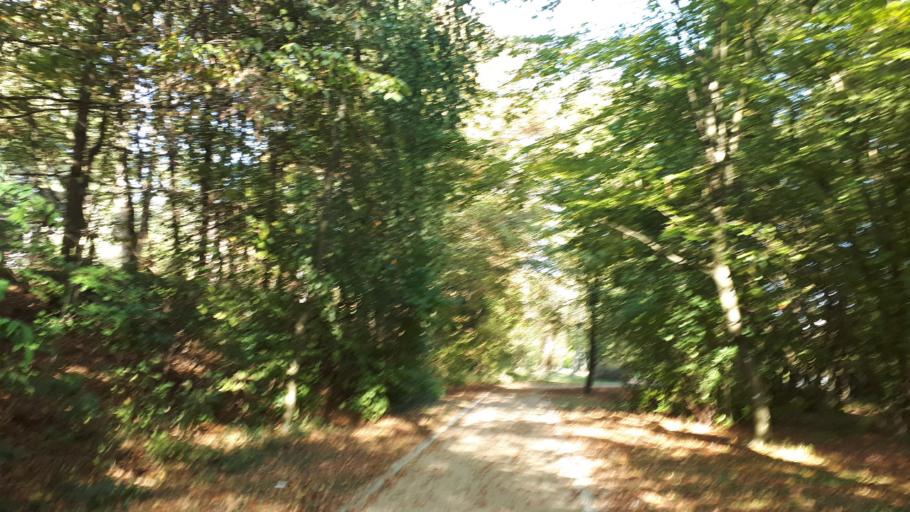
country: LU
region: Luxembourg
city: Kirchberg
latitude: 49.6307
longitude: 6.1634
